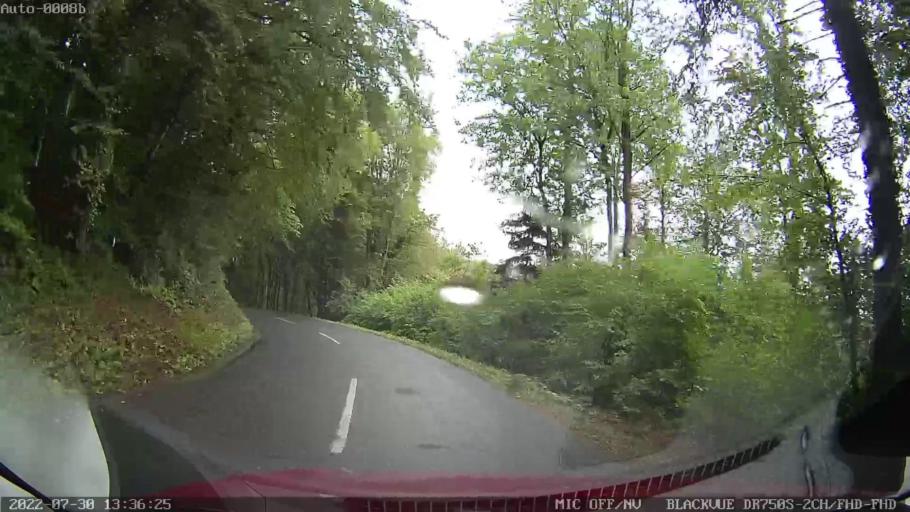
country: SI
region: Zuzemberk
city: Zuzemberk
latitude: 45.8701
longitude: 14.9249
